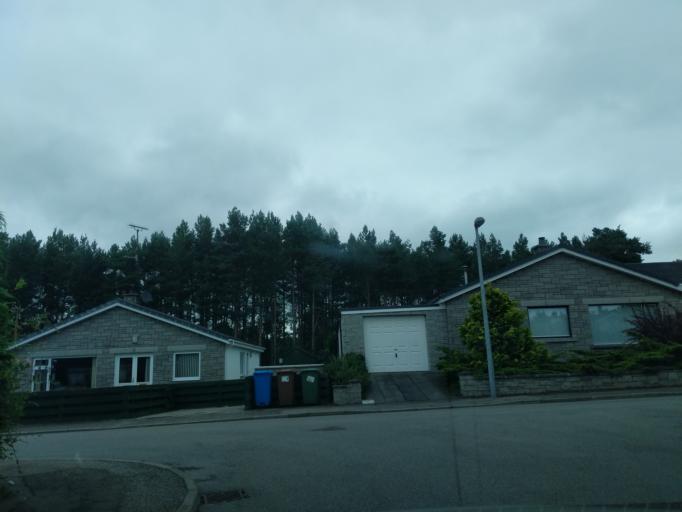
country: GB
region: Scotland
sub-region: Highland
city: Grantown on Spey
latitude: 57.3330
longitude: -3.6112
